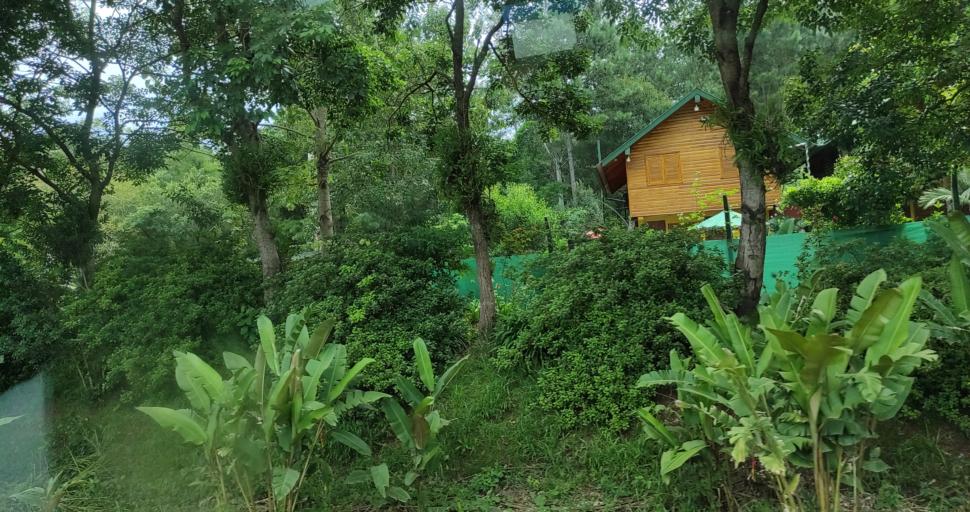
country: AR
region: Misiones
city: El Alcazar
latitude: -26.7058
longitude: -54.8180
